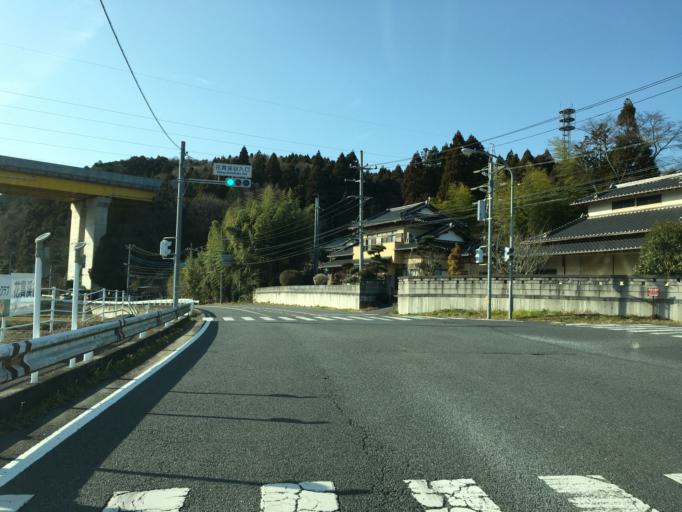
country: JP
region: Ibaraki
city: Takahagi
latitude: 36.7245
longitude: 140.6721
